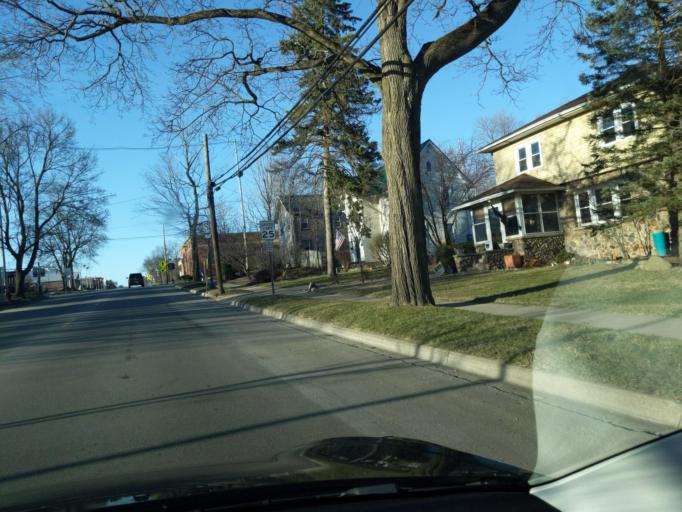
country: US
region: Michigan
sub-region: Washtenaw County
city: Chelsea
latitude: 42.3144
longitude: -84.0204
